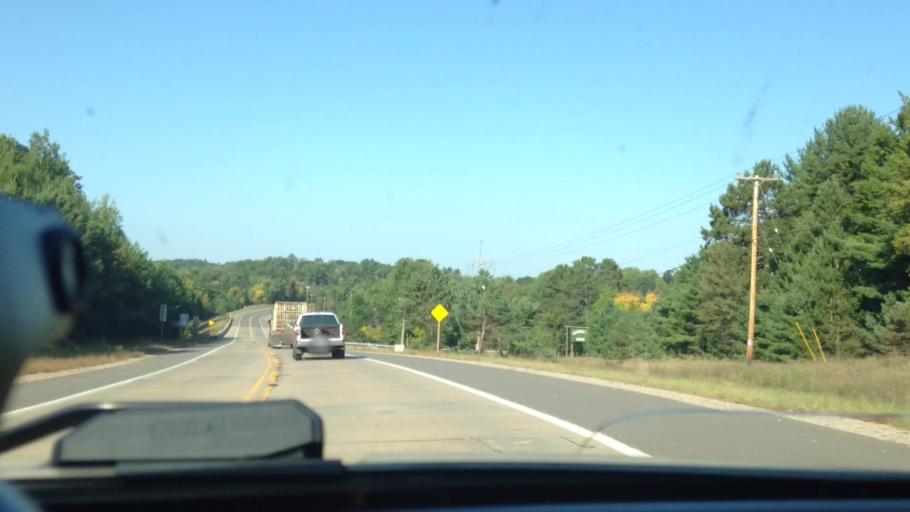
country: US
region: Michigan
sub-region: Dickinson County
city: Iron Mountain
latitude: 45.8662
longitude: -88.0708
